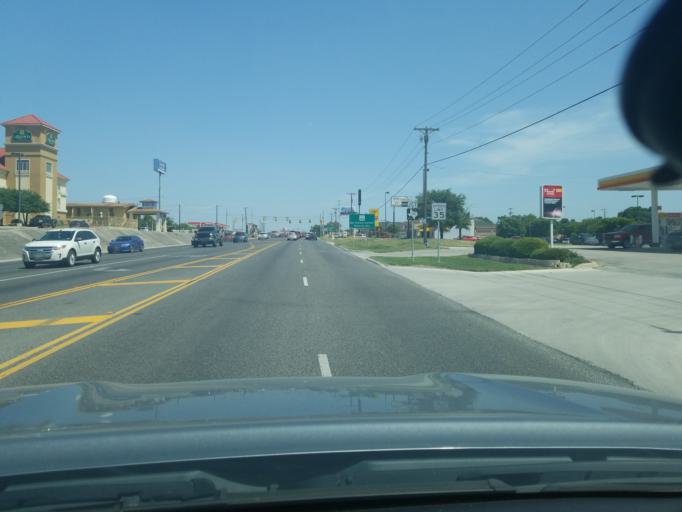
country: US
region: Texas
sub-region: Comal County
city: New Braunfels
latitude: 29.6997
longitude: -98.0931
